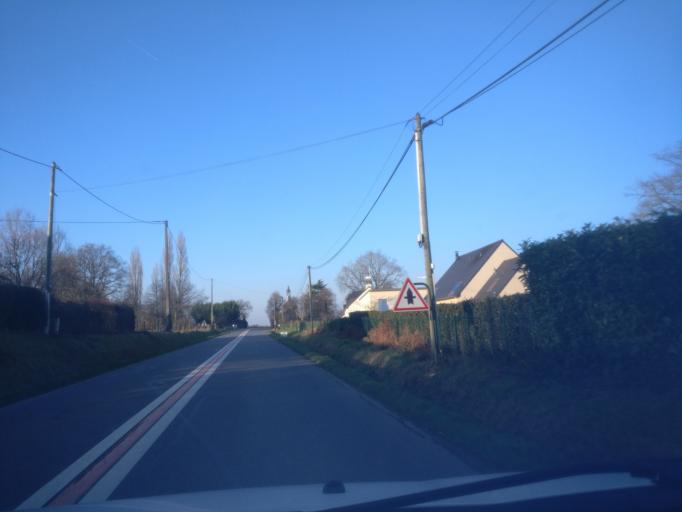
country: FR
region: Brittany
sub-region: Departement d'Ille-et-Vilaine
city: Livre-sur-Changeon
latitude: 48.2001
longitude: -1.3314
